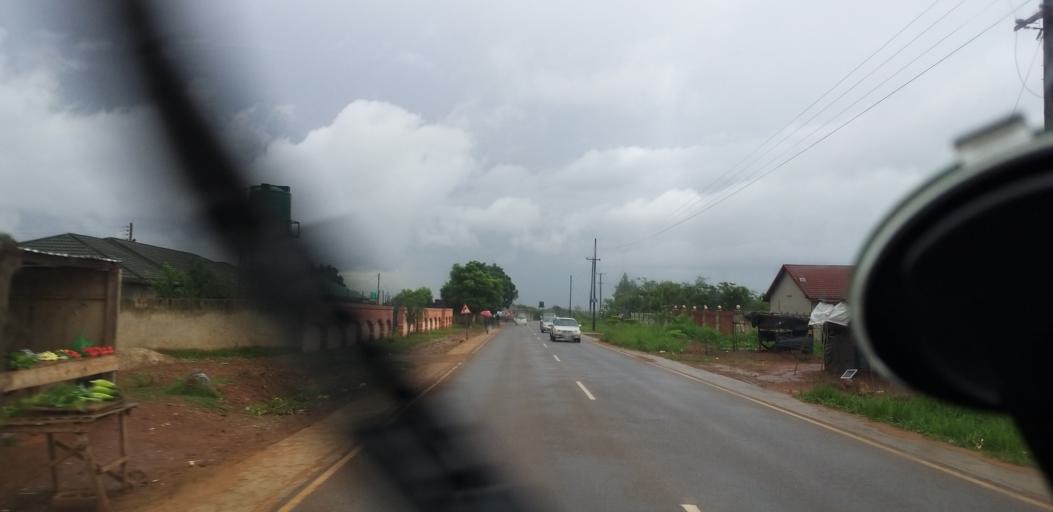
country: ZM
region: Lusaka
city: Lusaka
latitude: -15.4968
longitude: 28.3127
